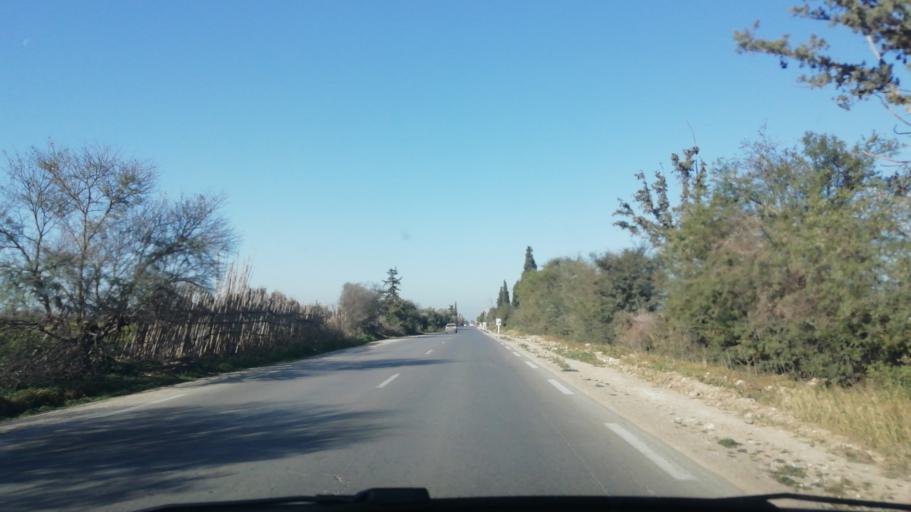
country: DZ
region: Mascara
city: Sig
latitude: 35.5709
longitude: -0.0361
